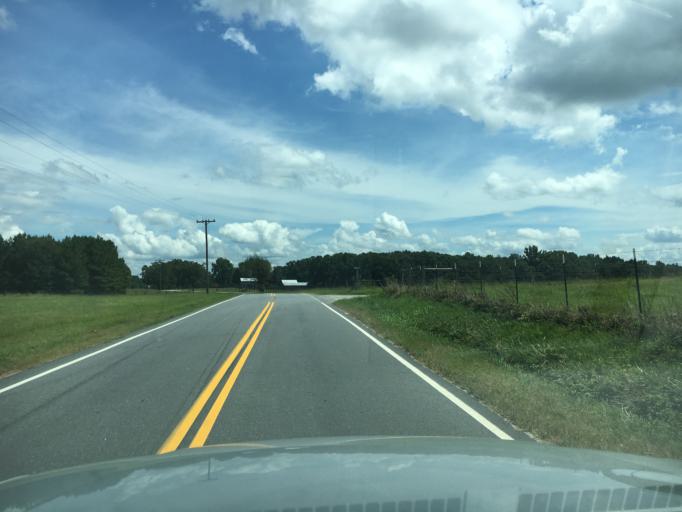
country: US
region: South Carolina
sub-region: Anderson County
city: Belton
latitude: 34.5233
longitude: -82.4287
